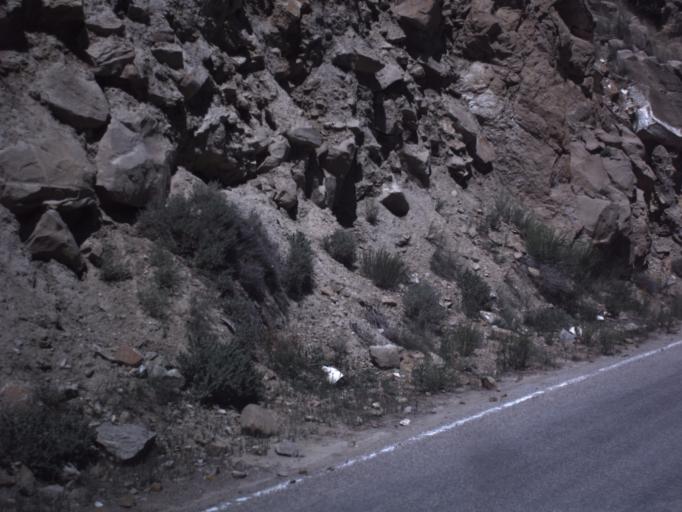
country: US
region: Utah
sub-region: Emery County
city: Orangeville
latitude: 39.2744
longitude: -111.2156
